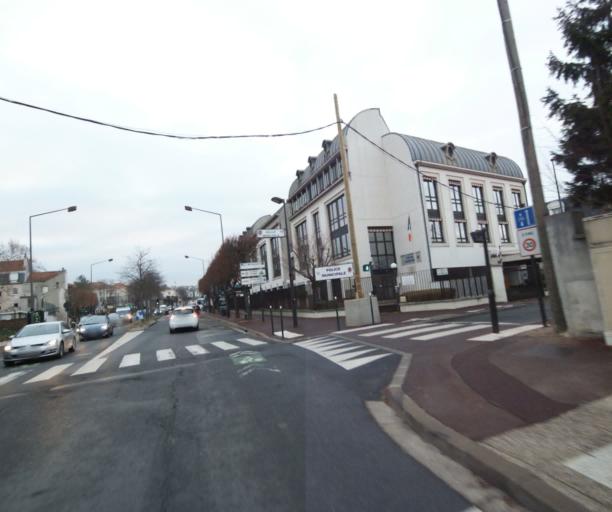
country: FR
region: Ile-de-France
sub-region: Departement des Hauts-de-Seine
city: Rueil-Malmaison
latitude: 48.8820
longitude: 2.1836
